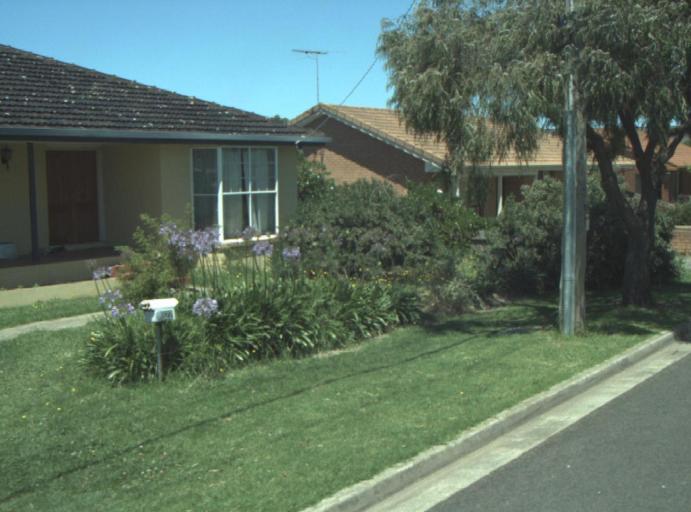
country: AU
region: Victoria
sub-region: Queenscliffe
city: Queenscliff
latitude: -38.1729
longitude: 144.7130
